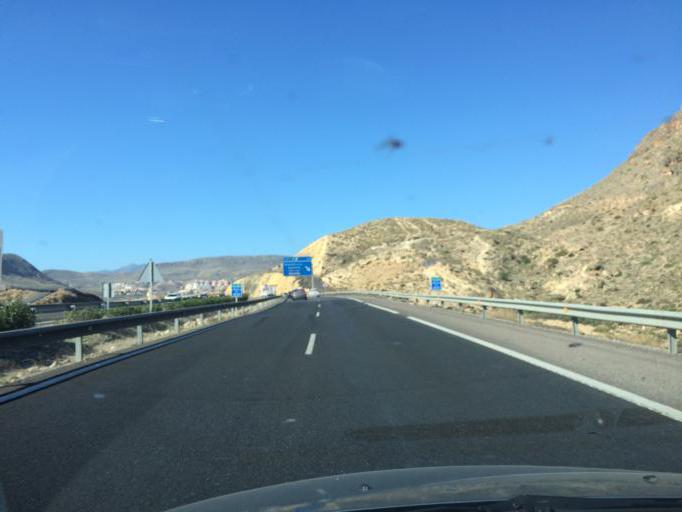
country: ES
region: Andalusia
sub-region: Provincia de Almeria
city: Aguadulce
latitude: 36.8265
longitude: -2.5822
